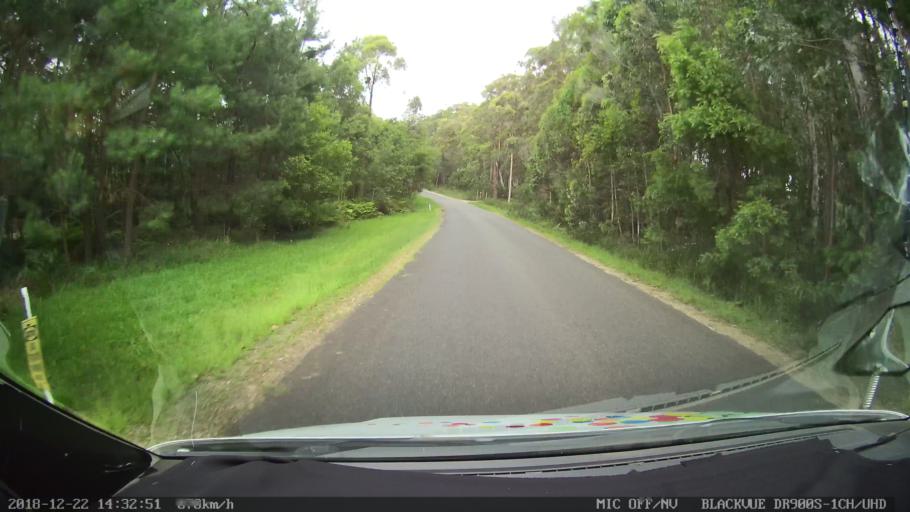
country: AU
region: New South Wales
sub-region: Bellingen
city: Dorrigo
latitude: -30.1076
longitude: 152.6241
